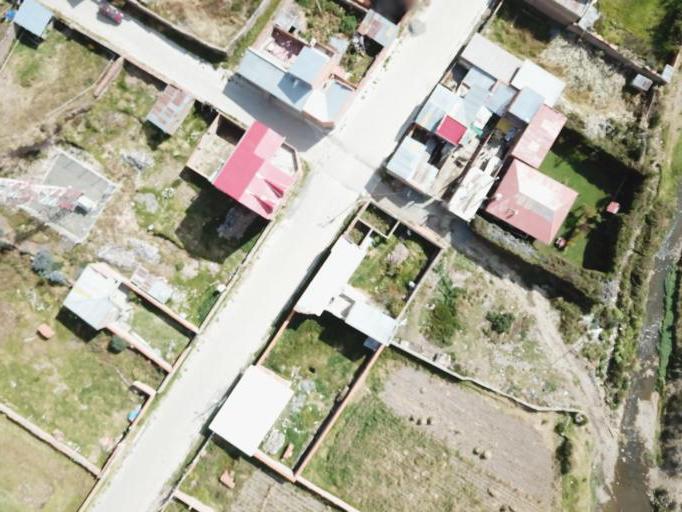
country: BO
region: La Paz
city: Achacachi
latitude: -16.0553
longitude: -68.8169
